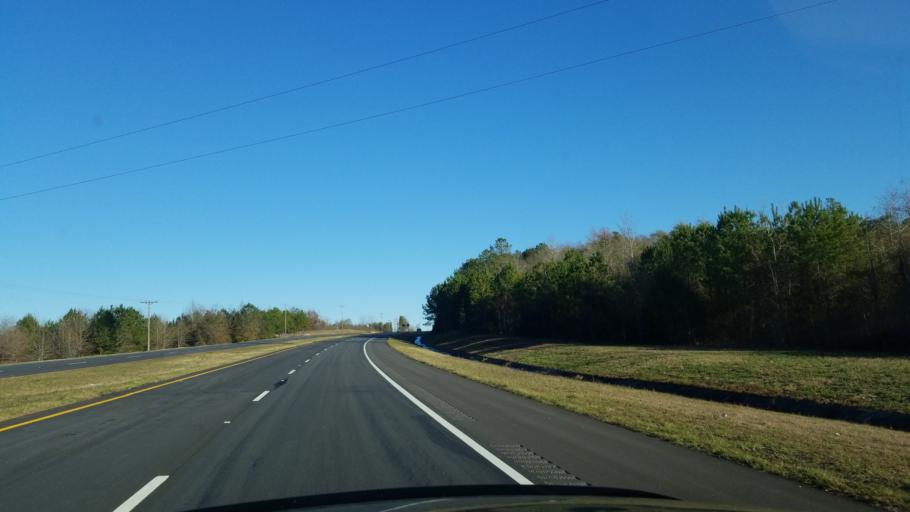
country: US
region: Georgia
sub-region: Talbot County
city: Talbotton
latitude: 32.5755
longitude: -84.5710
